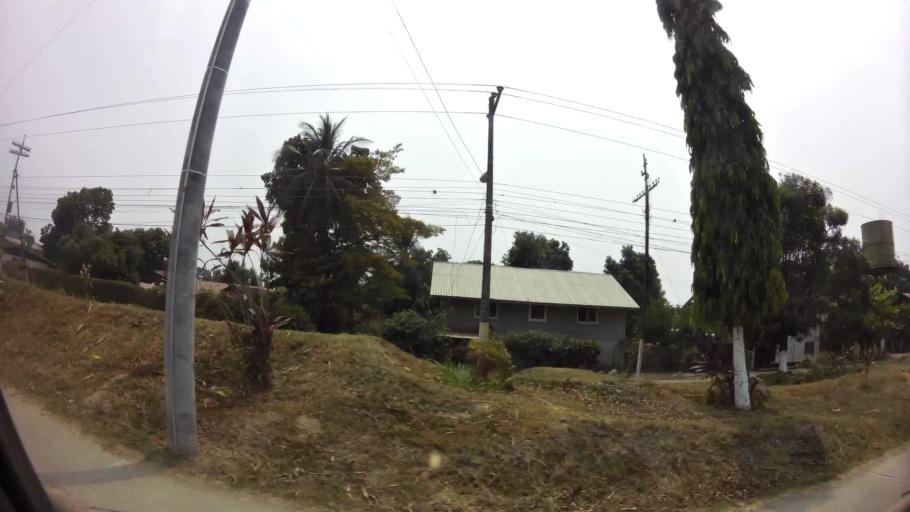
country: HN
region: Yoro
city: El Progreso
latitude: 15.3952
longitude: -87.8119
